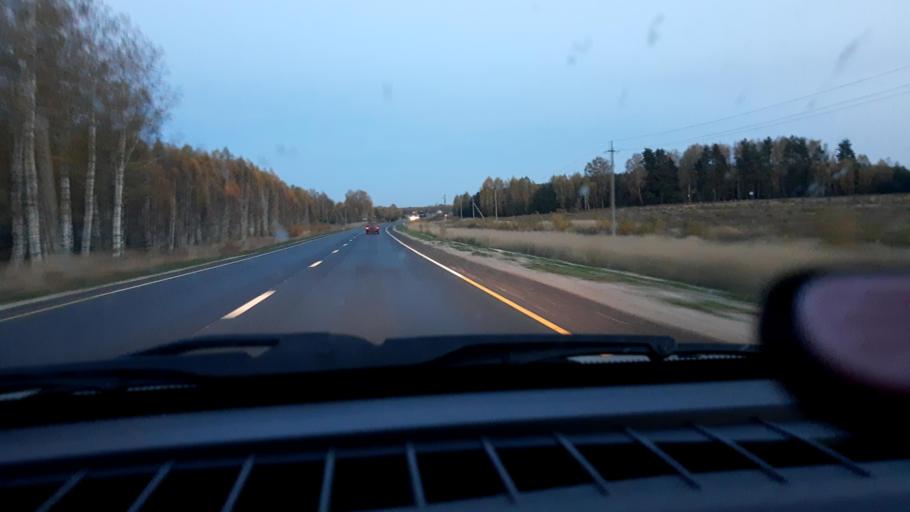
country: RU
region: Nizjnij Novgorod
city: Novaya Balakhna
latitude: 56.6125
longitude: 43.5953
